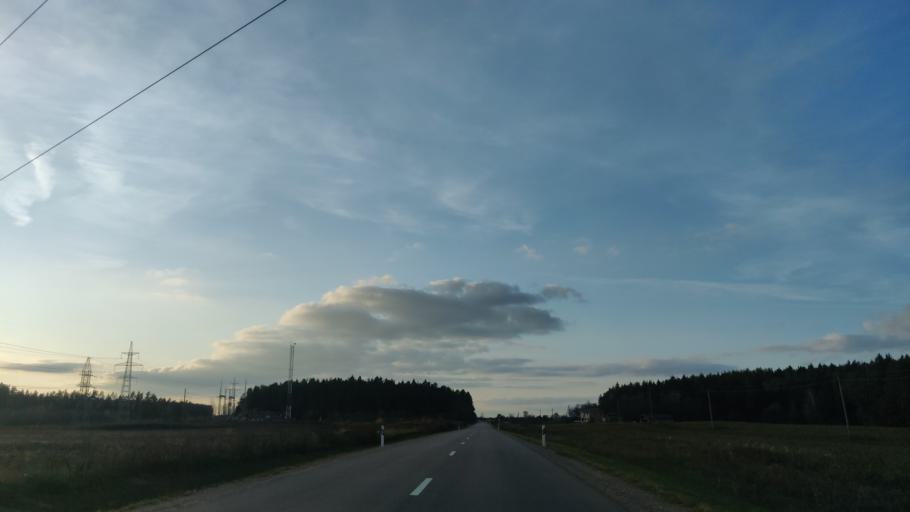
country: LT
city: Lentvaris
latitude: 54.5967
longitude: 25.0322
